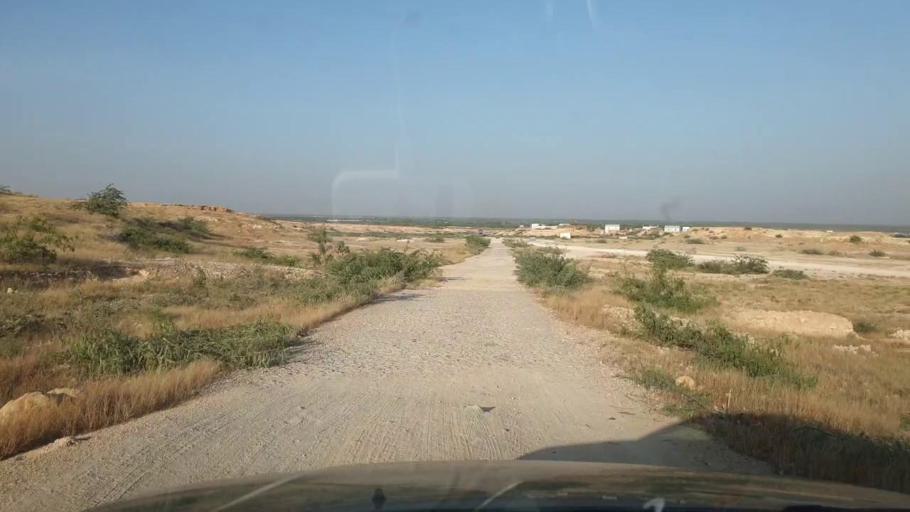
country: PK
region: Sindh
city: Kotri
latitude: 25.2107
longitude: 68.2156
